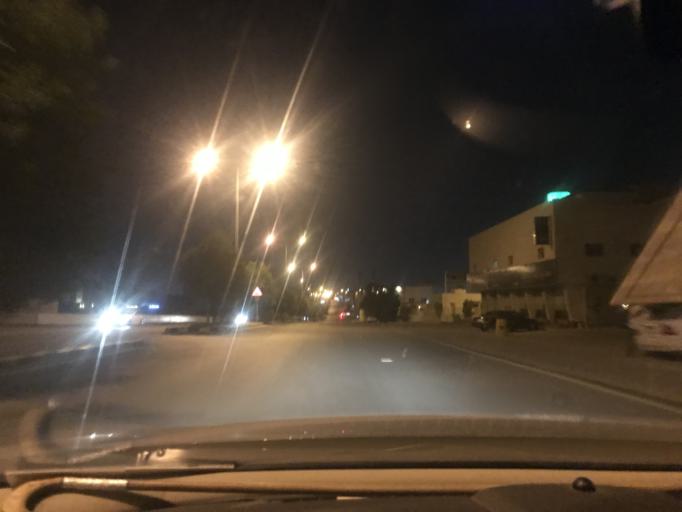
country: SA
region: Ar Riyad
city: Riyadh
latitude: 24.7542
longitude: 46.7547
